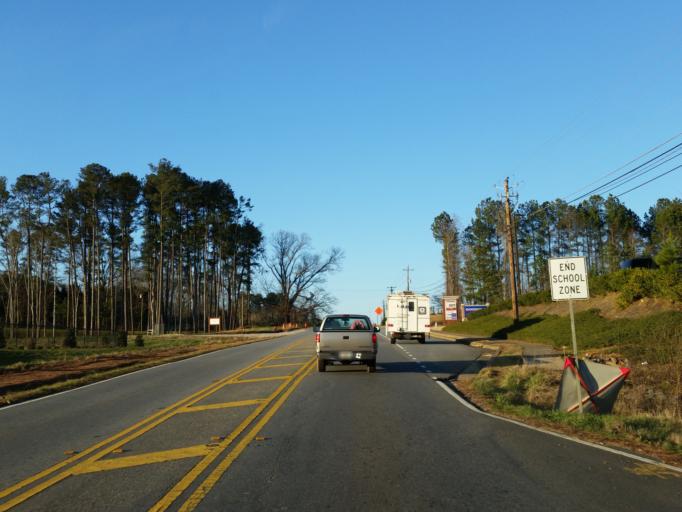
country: US
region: Georgia
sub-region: Cherokee County
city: Holly Springs
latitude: 34.1727
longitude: -84.4216
